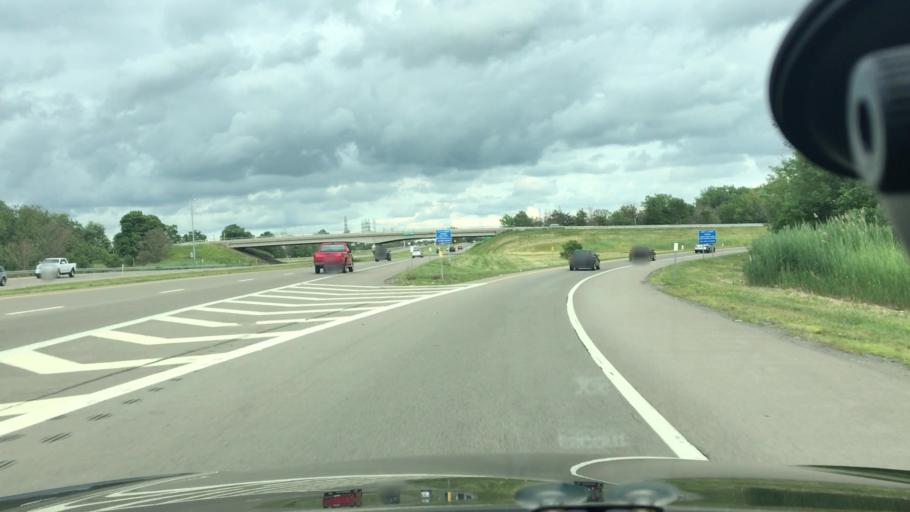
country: US
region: New York
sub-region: Erie County
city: West Seneca
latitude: 42.8489
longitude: -78.7836
